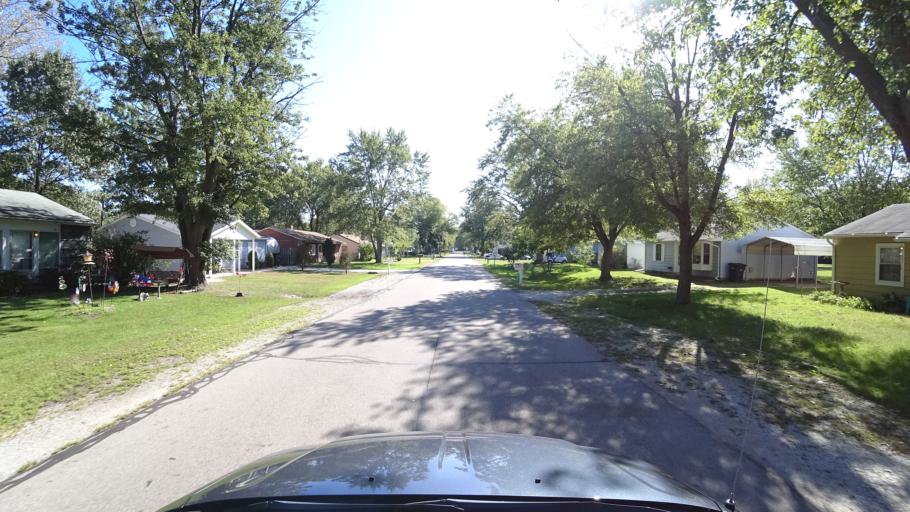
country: US
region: Indiana
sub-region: LaPorte County
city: Michigan City
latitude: 41.6943
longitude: -86.8991
